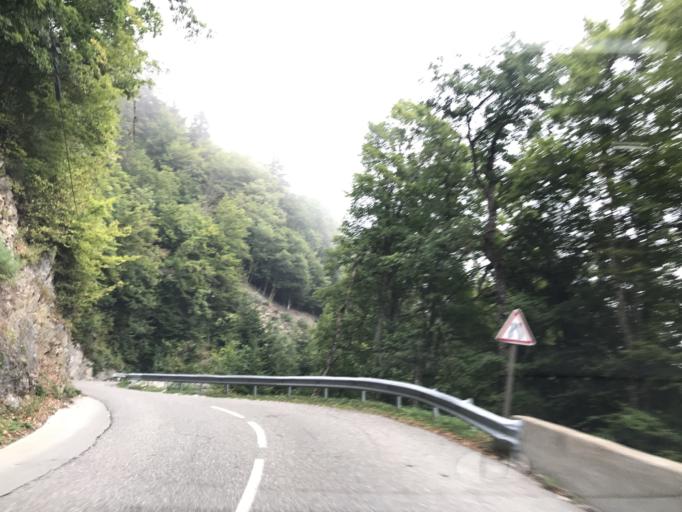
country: FR
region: Rhone-Alpes
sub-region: Departement de la Haute-Savoie
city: Talloires
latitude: 45.8189
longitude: 6.2428
